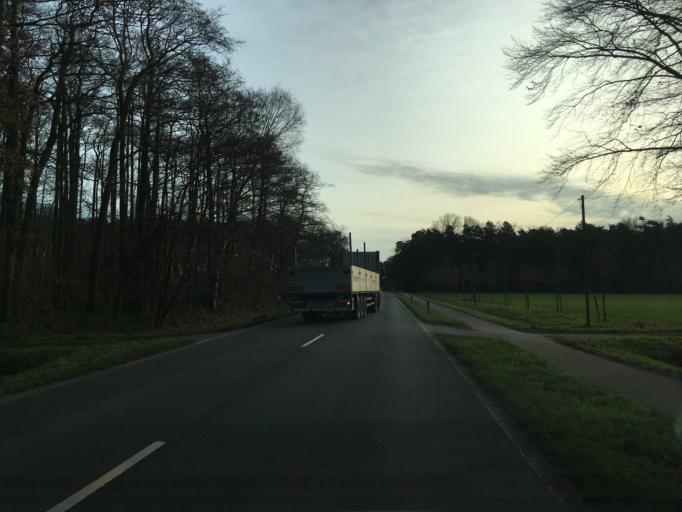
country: DE
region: North Rhine-Westphalia
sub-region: Regierungsbezirk Munster
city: Ahaus
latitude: 52.0496
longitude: 7.0141
